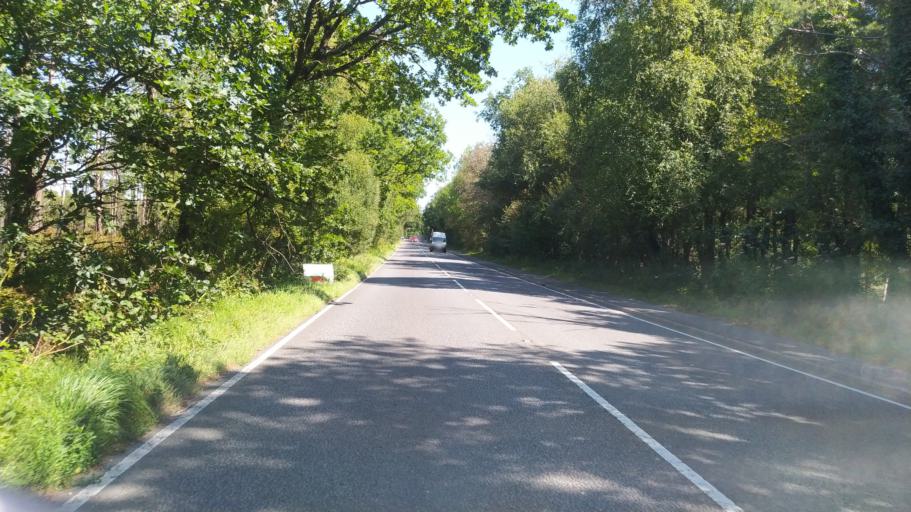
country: GB
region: England
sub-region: Dorset
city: Lytchett Matravers
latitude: 50.7258
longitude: -2.0743
